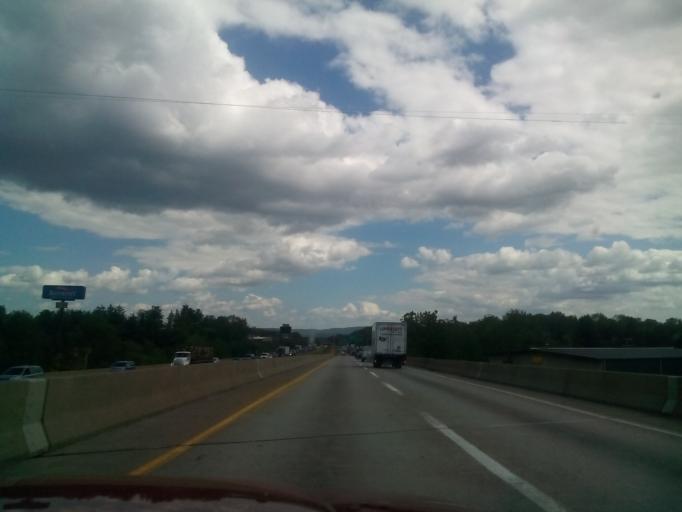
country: US
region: Pennsylvania
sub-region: Monroe County
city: Tannersville
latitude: 41.0028
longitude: -75.2800
